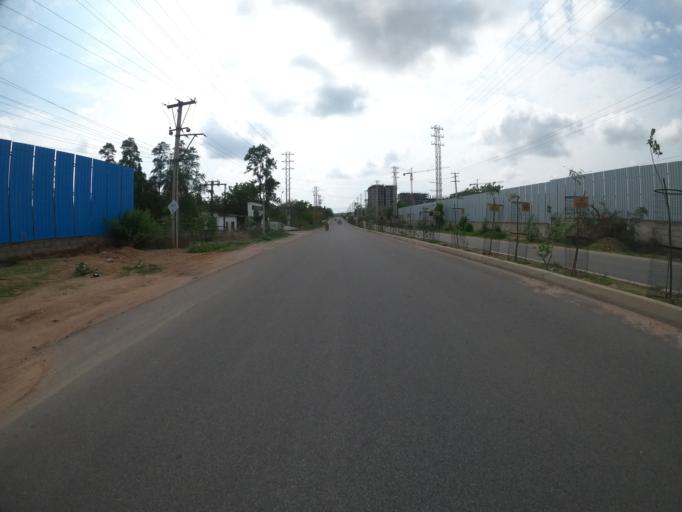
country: IN
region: Telangana
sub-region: Medak
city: Serilingampalle
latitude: 17.3903
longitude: 78.3256
